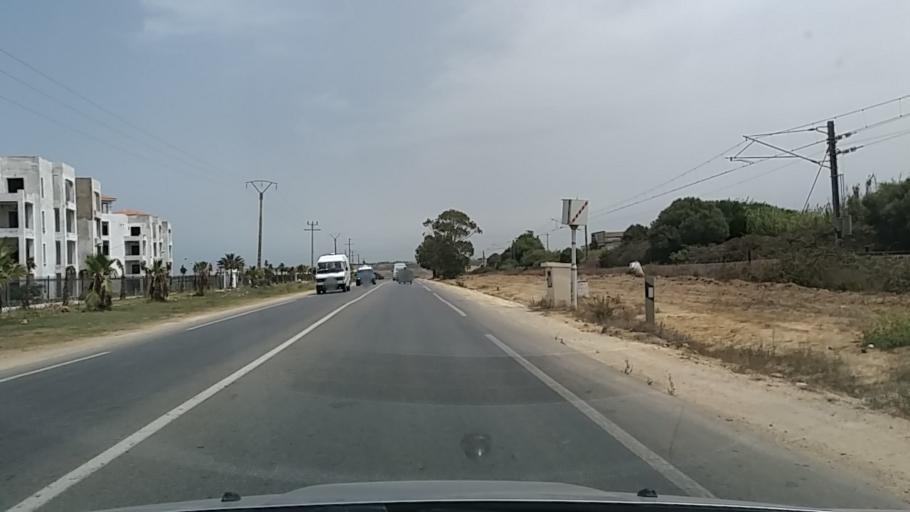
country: MA
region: Tanger-Tetouan
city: Asilah
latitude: 35.4958
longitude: -6.0153
